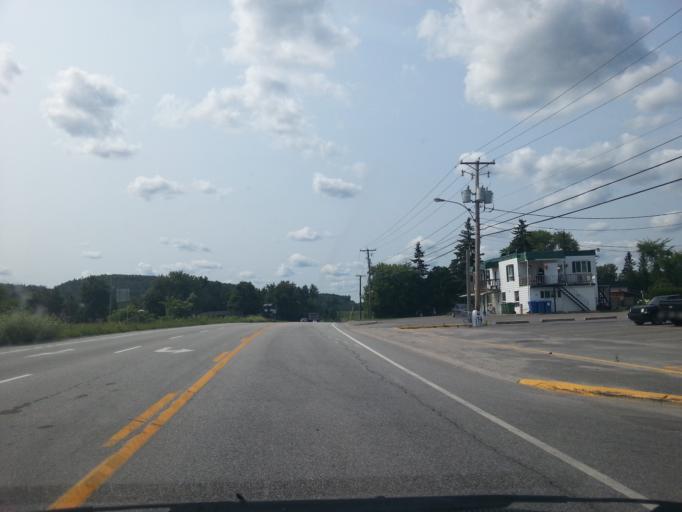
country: CA
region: Quebec
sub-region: Outaouais
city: Wakefield
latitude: 45.5962
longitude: -75.8959
